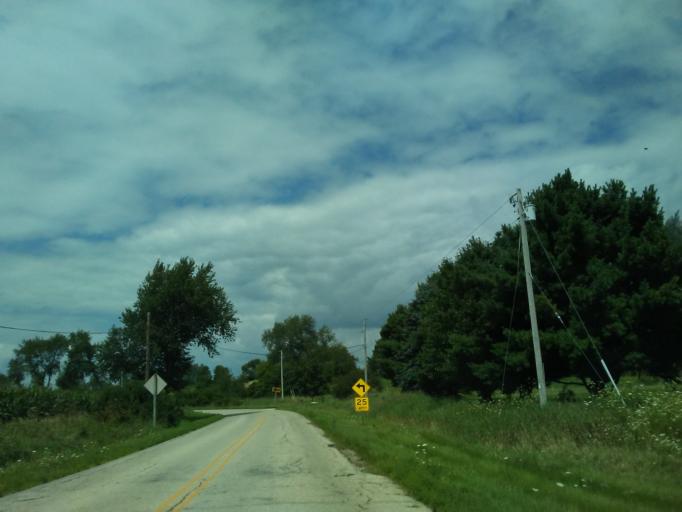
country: US
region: Wisconsin
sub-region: Dane County
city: Verona
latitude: 42.9919
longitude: -89.5728
